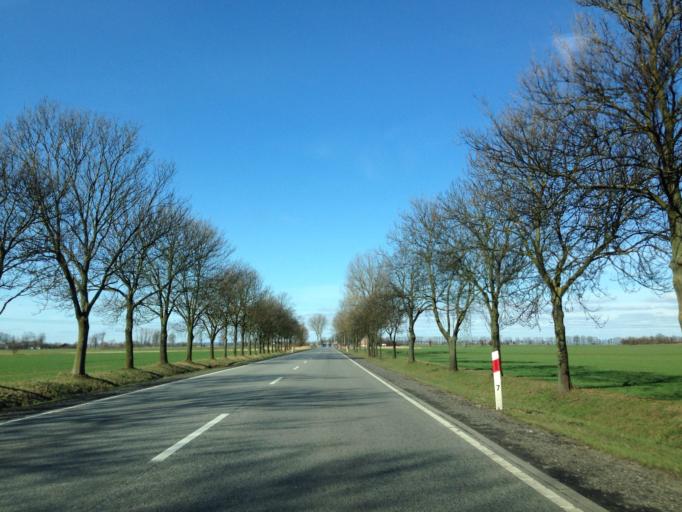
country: PL
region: Pomeranian Voivodeship
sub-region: Powiat malborski
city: Miloradz
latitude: 54.0483
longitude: 18.9533
